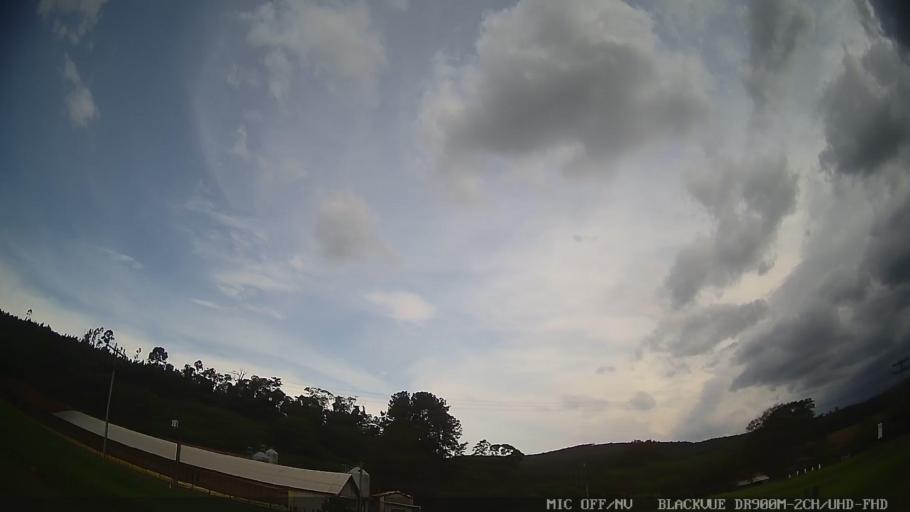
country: BR
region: Sao Paulo
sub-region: Amparo
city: Amparo
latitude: -22.8104
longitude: -46.7556
